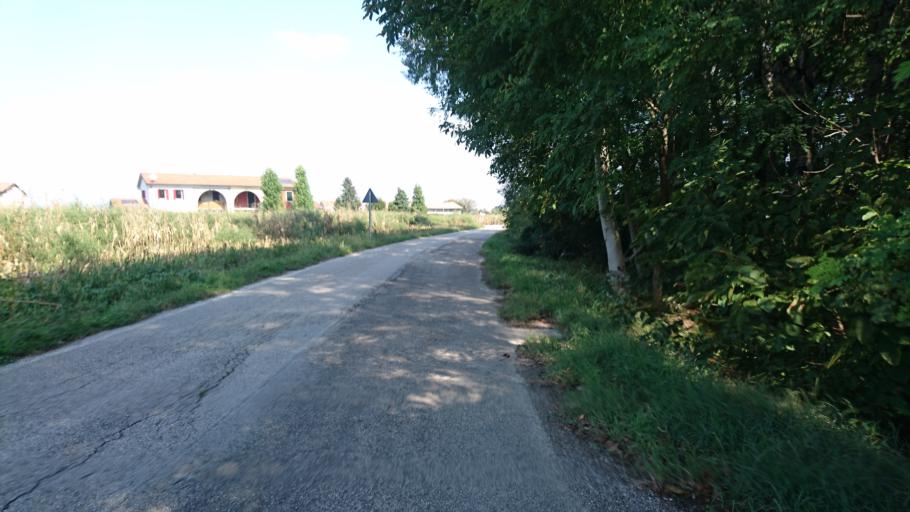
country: IT
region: Veneto
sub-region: Provincia di Padova
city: Piazzola sul Brenta
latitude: 45.5701
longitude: 11.7801
